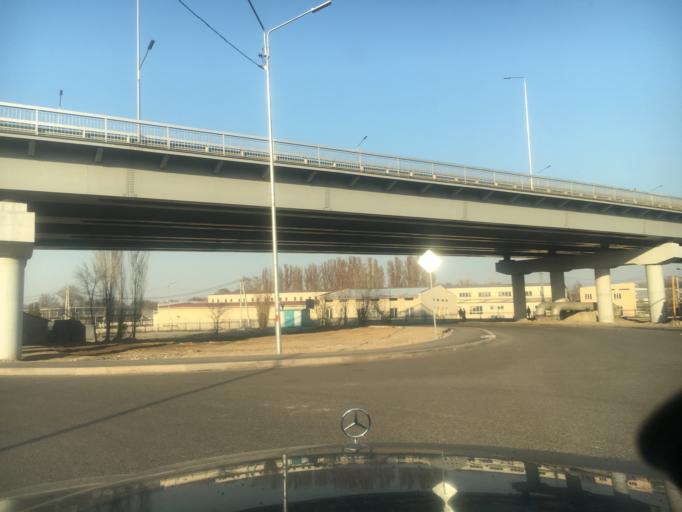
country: KZ
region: Almaty Qalasy
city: Almaty
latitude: 43.2765
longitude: 76.9427
